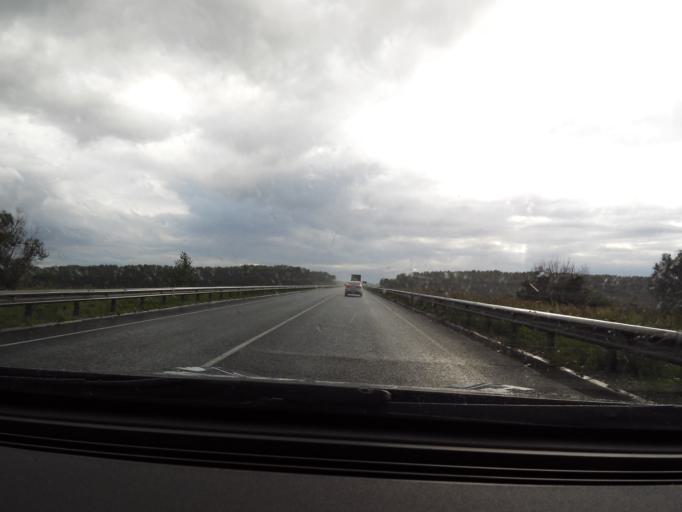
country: RU
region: Tatarstan
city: Nizhniye Vyazovyye
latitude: 55.7251
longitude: 48.4898
